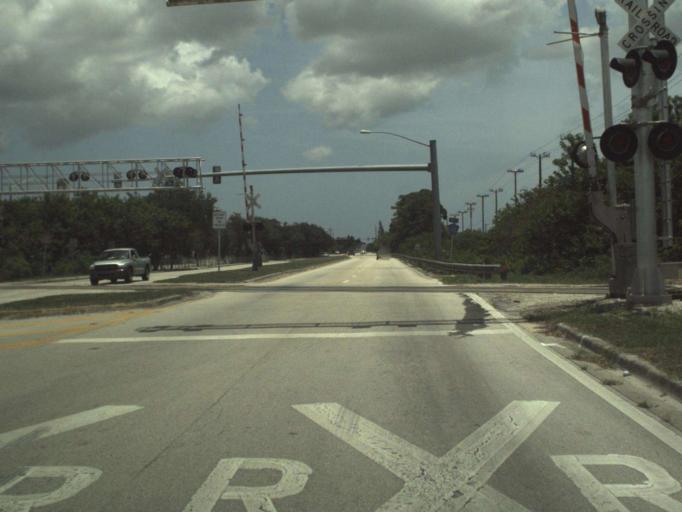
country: US
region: Florida
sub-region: Saint Lucie County
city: Fort Pierce South
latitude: 27.3744
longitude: -80.3923
